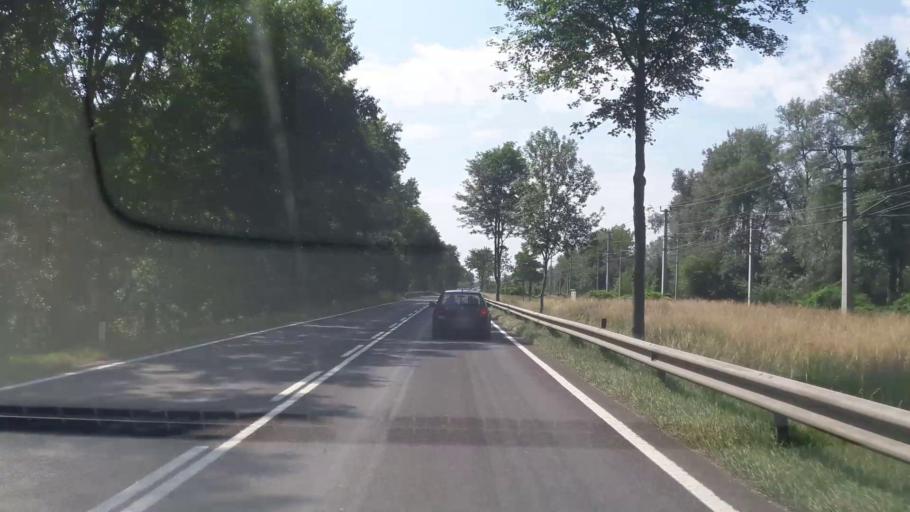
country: AT
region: Lower Austria
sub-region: Politischer Bezirk Tulln
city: Tulln
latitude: 48.3480
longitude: 16.0594
